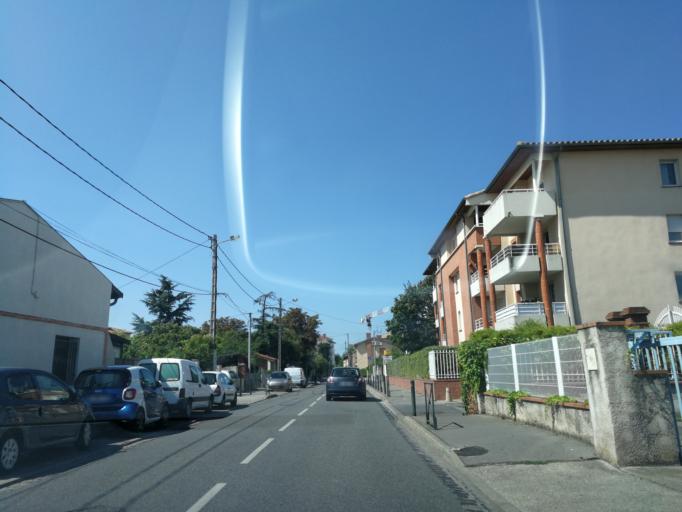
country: FR
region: Midi-Pyrenees
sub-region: Departement de la Haute-Garonne
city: L'Union
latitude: 43.6341
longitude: 1.4678
